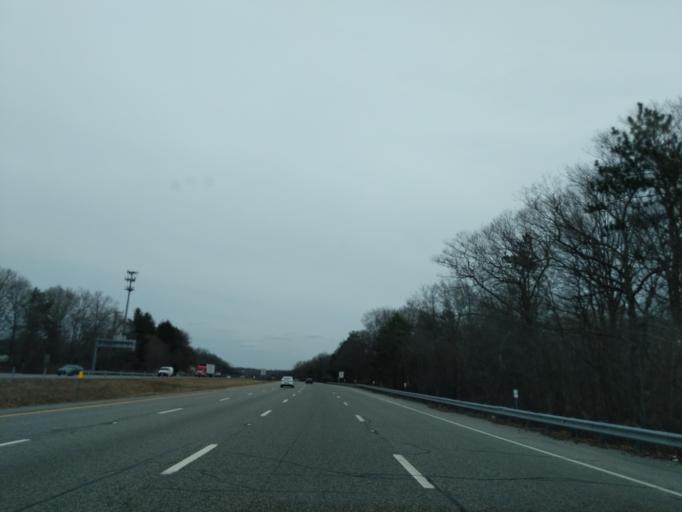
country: US
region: Rhode Island
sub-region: Providence County
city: Cumberland
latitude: 41.9506
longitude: -71.3985
